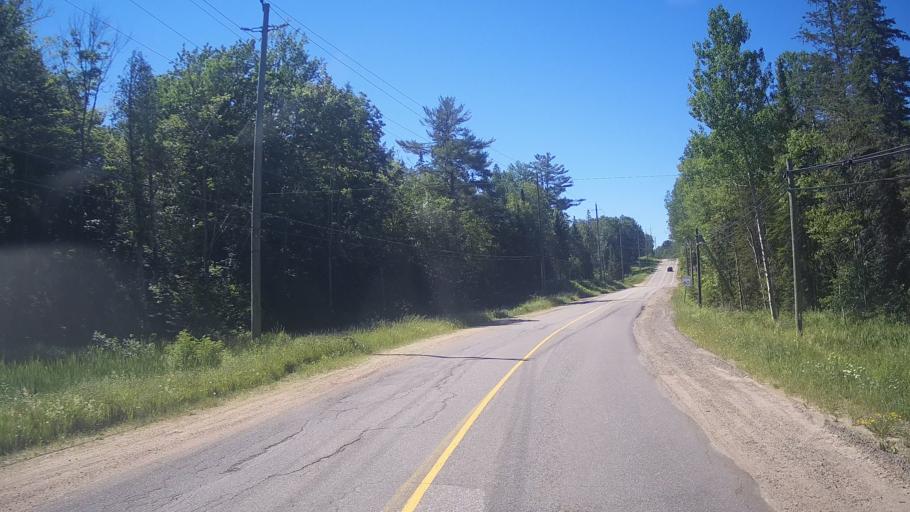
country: CA
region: Ontario
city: Huntsville
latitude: 45.3680
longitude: -79.2049
